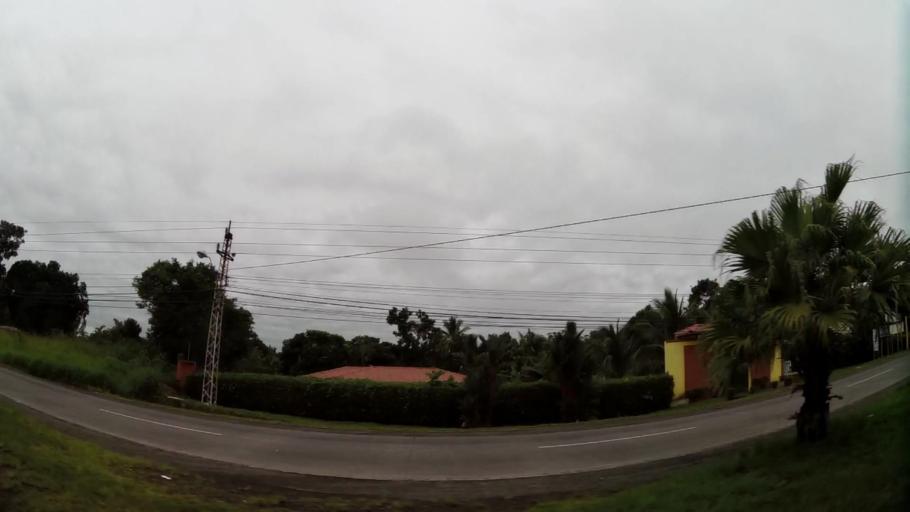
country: PA
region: Chiriqui
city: Boqueron
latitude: 8.4956
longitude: -82.5872
